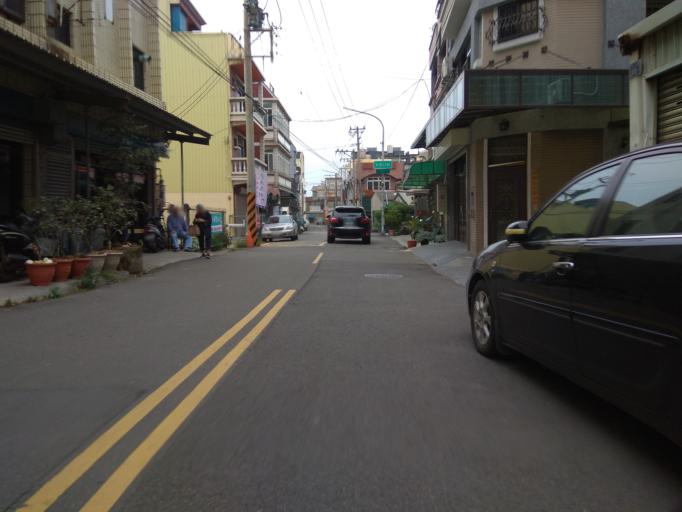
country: TW
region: Taiwan
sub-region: Hsinchu
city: Hsinchu
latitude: 24.7932
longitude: 120.9229
